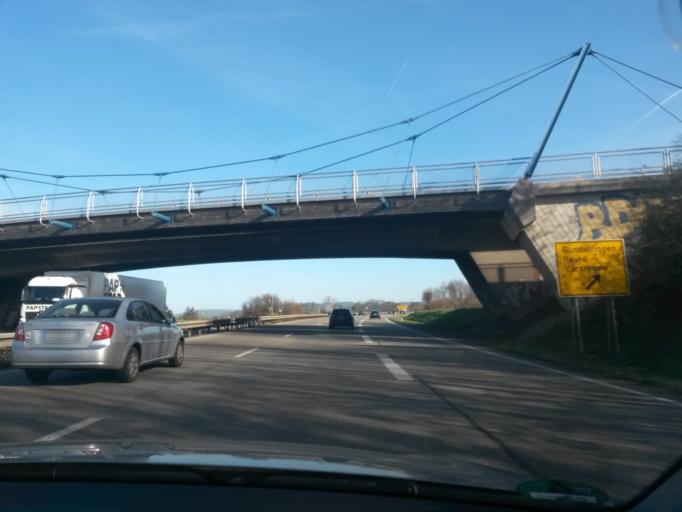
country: DE
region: Baden-Wuerttemberg
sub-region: Freiburg Region
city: Gundelfingen
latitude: 48.0501
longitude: 7.8592
